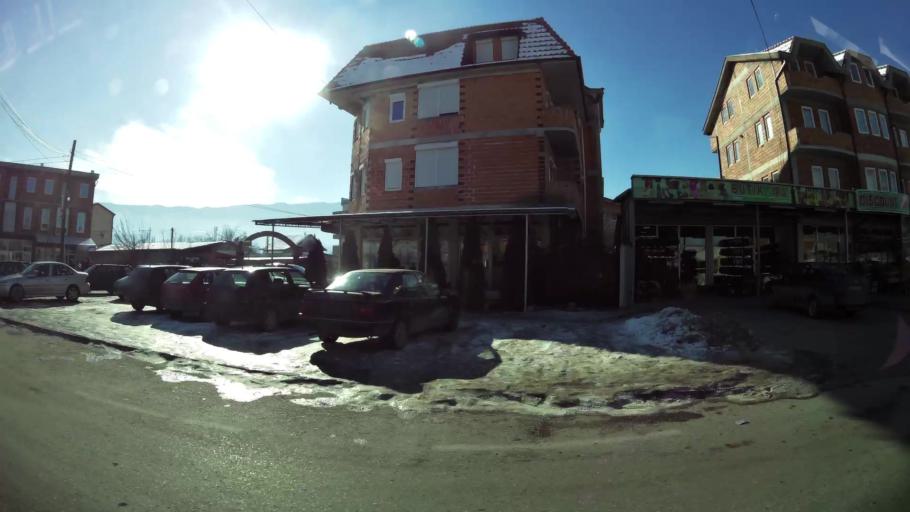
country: MK
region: Saraj
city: Saraj
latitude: 41.9999
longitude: 21.3278
